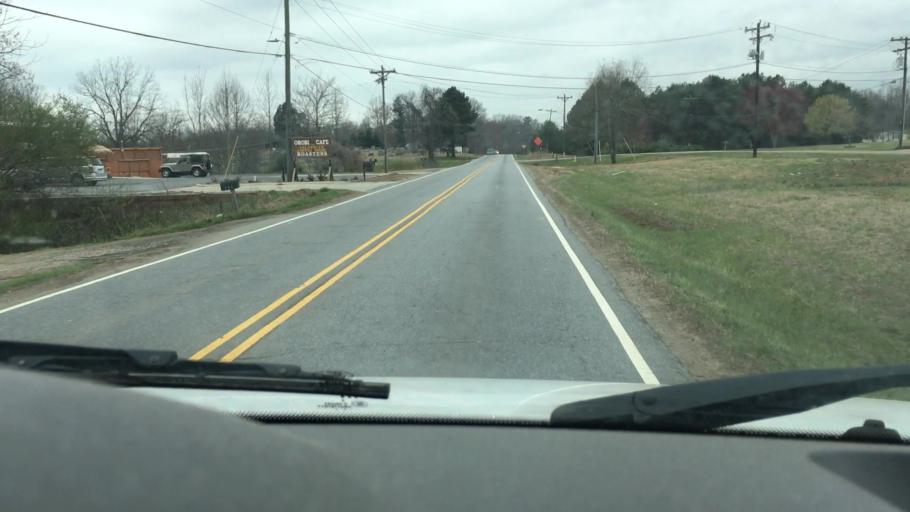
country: US
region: North Carolina
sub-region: Iredell County
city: Troutman
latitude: 35.6901
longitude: -80.8682
